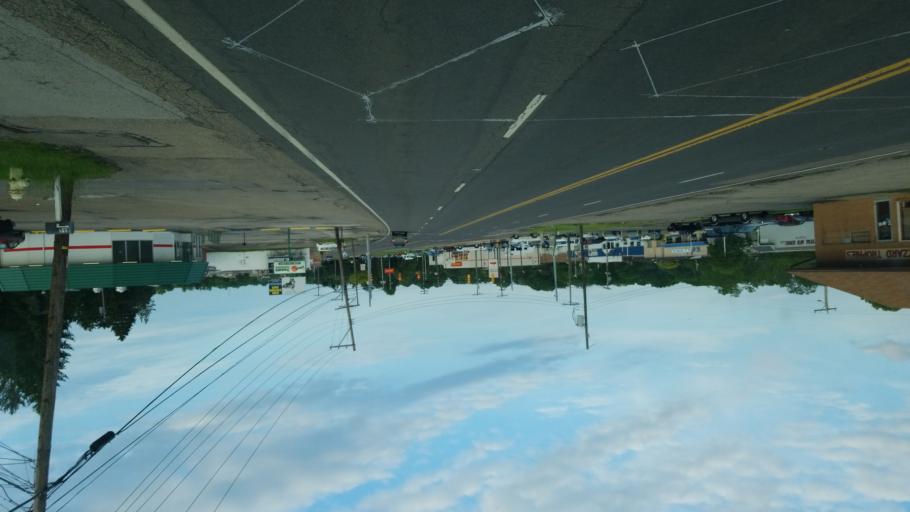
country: US
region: Ohio
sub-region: Summit County
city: Sawyerwood
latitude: 41.0400
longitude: -81.4339
